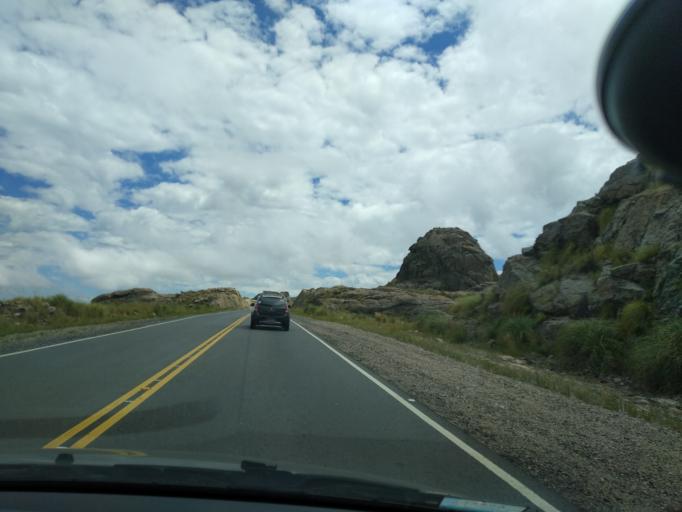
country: AR
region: Cordoba
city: Mina Clavero
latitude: -31.6741
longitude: -64.8998
